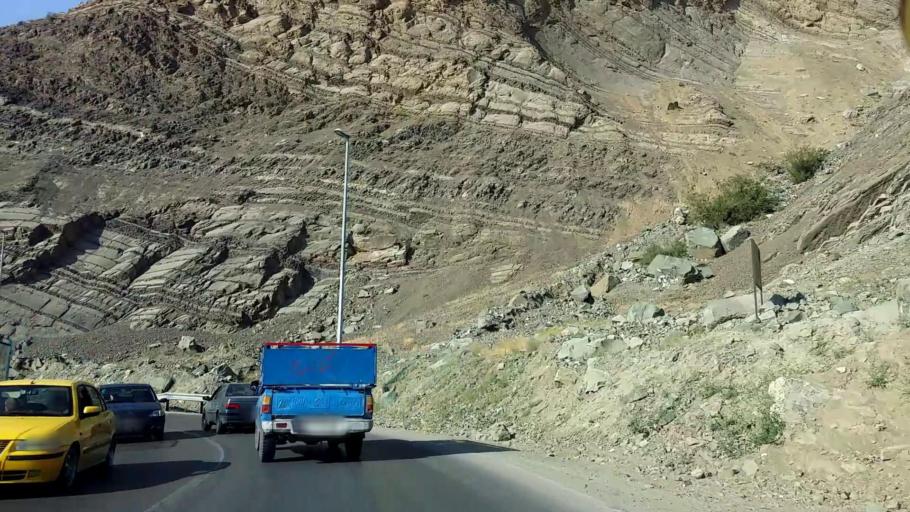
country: IR
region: Alborz
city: Karaj
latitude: 35.9676
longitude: 51.0933
